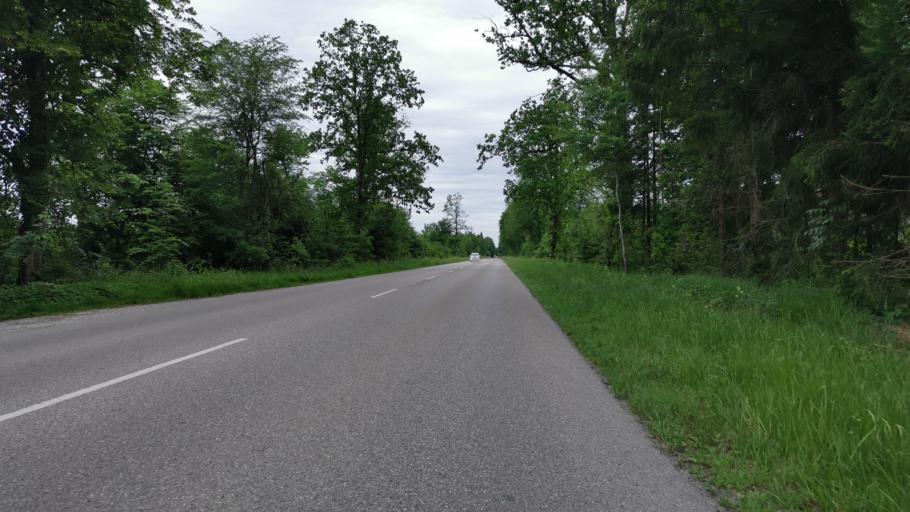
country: DE
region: Bavaria
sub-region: Upper Bavaria
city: Krailling
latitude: 48.1072
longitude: 11.3743
